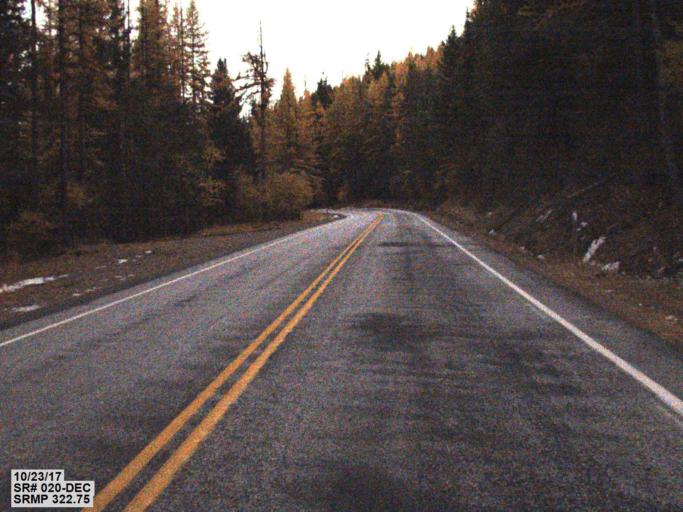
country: US
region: Washington
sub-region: Ferry County
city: Republic
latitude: 48.6163
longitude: -118.4441
